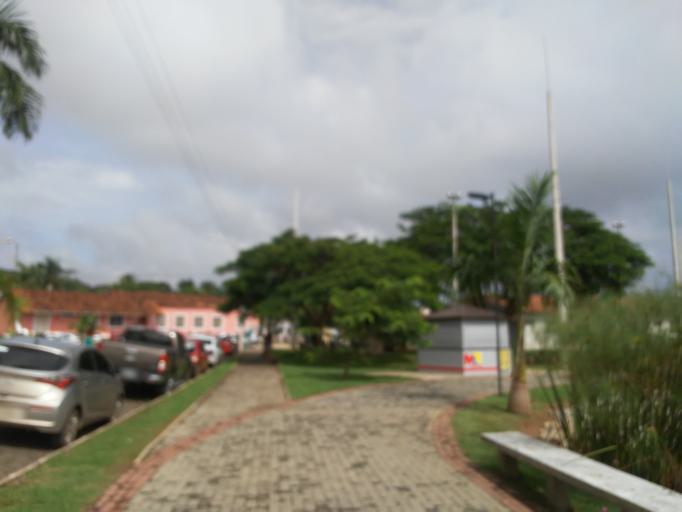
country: BR
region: Goias
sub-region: Ipameri
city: Ipameri
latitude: -17.7203
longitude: -48.1666
